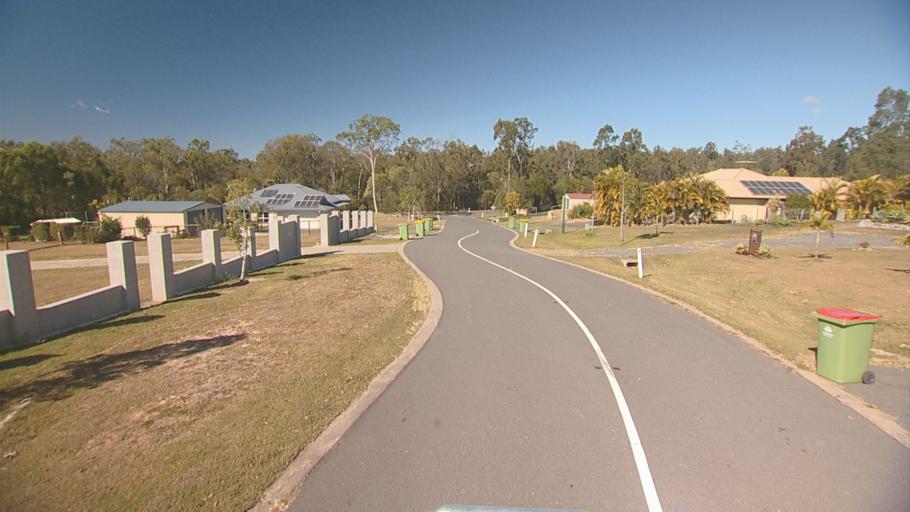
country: AU
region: Queensland
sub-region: Logan
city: North Maclean
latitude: -27.7559
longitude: 152.9600
